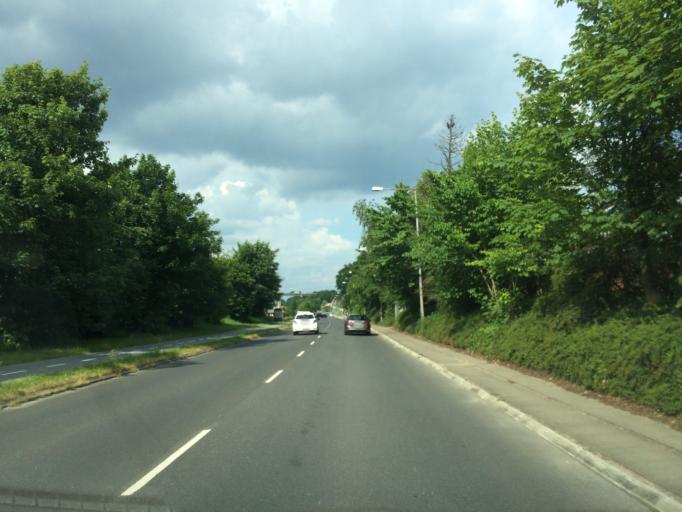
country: DK
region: South Denmark
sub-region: Middelfart Kommune
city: Middelfart
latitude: 55.5092
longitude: 9.7544
